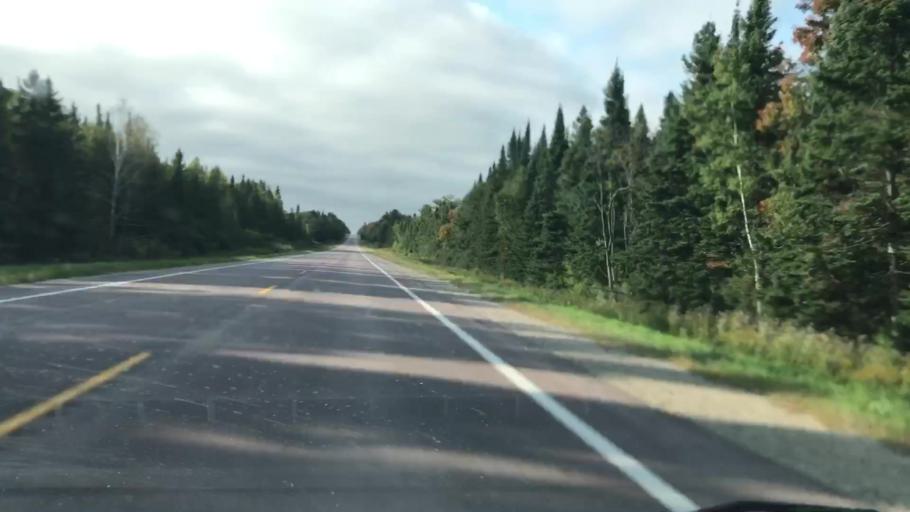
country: US
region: Michigan
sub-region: Luce County
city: Newberry
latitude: 46.2994
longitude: -85.5686
